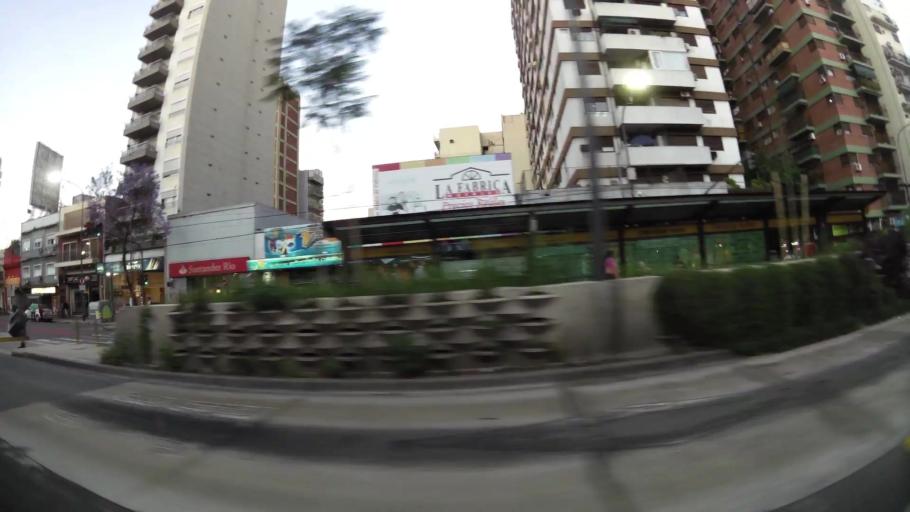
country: AR
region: Buenos Aires F.D.
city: Colegiales
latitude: -34.5519
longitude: -58.4659
